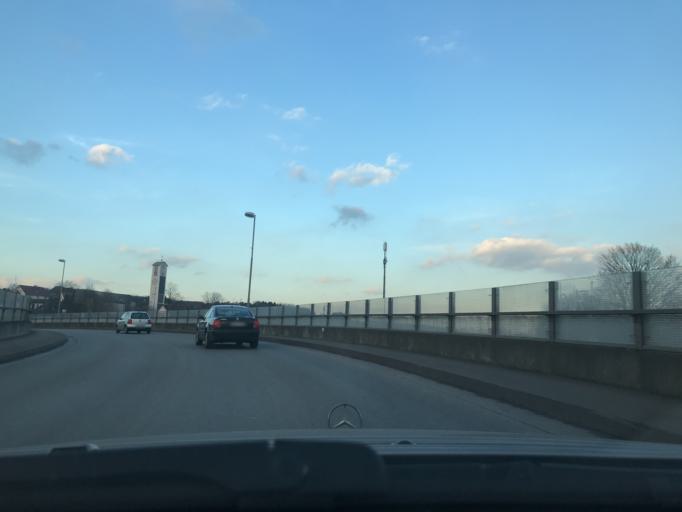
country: DE
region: North Rhine-Westphalia
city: Wickede
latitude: 51.4929
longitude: 7.8699
